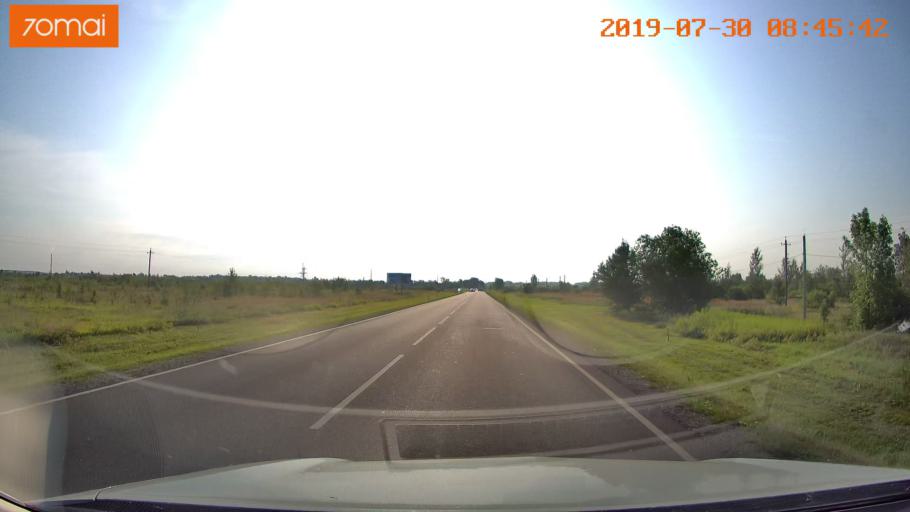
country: RU
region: Kaliningrad
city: Chernyakhovsk
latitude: 54.6260
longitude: 21.8685
